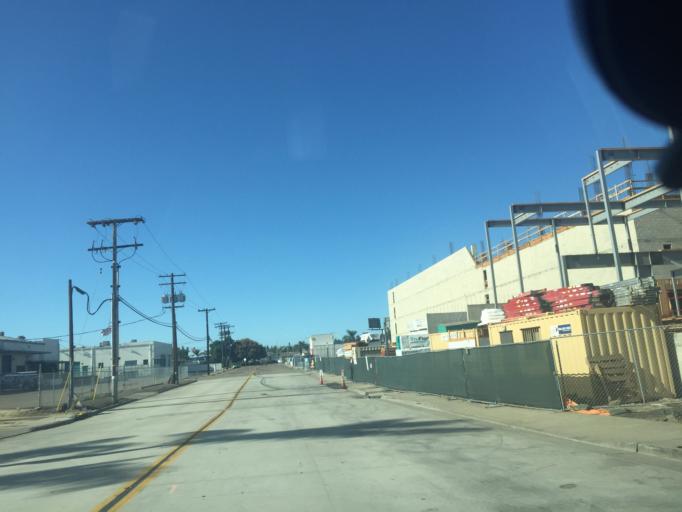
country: US
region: California
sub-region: San Diego County
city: La Mesa
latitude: 32.7830
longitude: -117.0958
